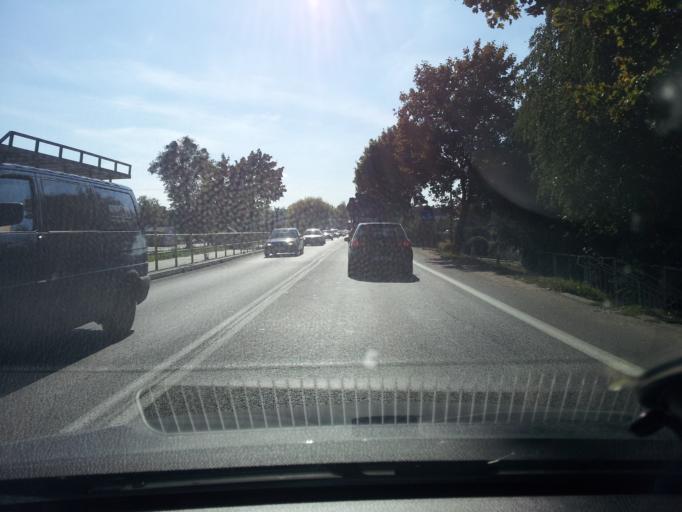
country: PL
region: Kujawsko-Pomorskie
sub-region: Powiat torunski
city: Lubicz Dolny
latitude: 53.0587
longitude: 18.7203
